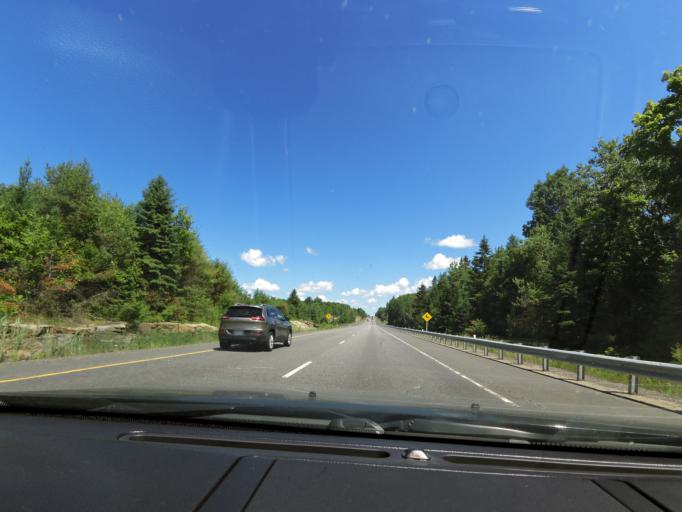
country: CA
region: Ontario
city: Bracebridge
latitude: 45.1390
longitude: -79.3109
